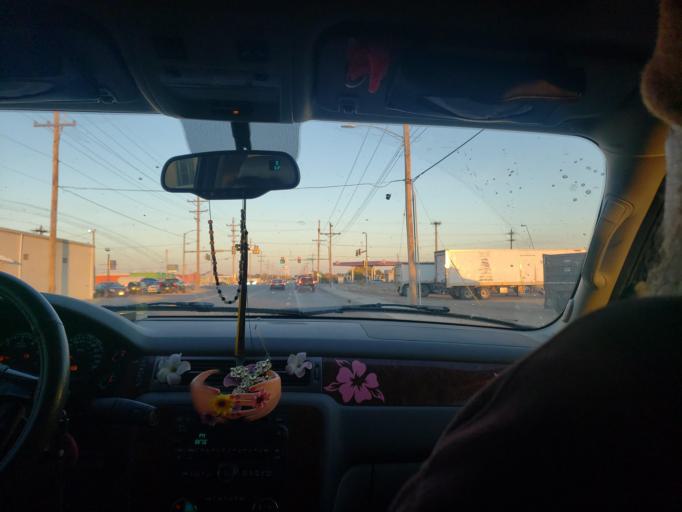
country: US
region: Kansas
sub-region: Finney County
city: Garden City
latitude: 37.9896
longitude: -100.8848
